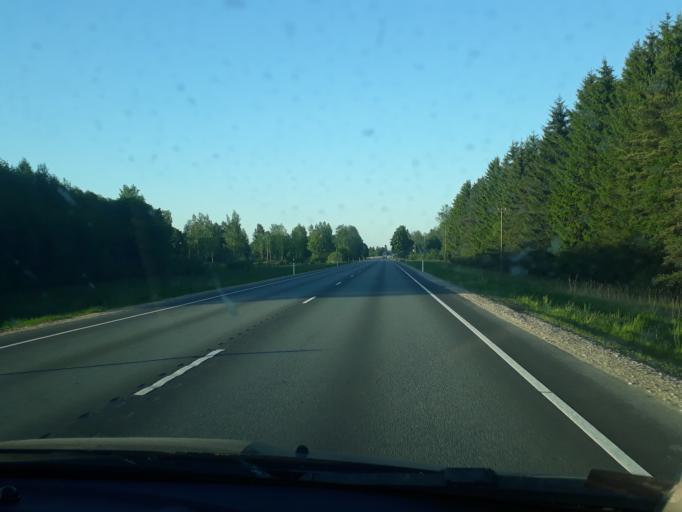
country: EE
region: Paernumaa
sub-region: Tootsi vald
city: Tootsi
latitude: 58.4883
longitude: 24.7522
